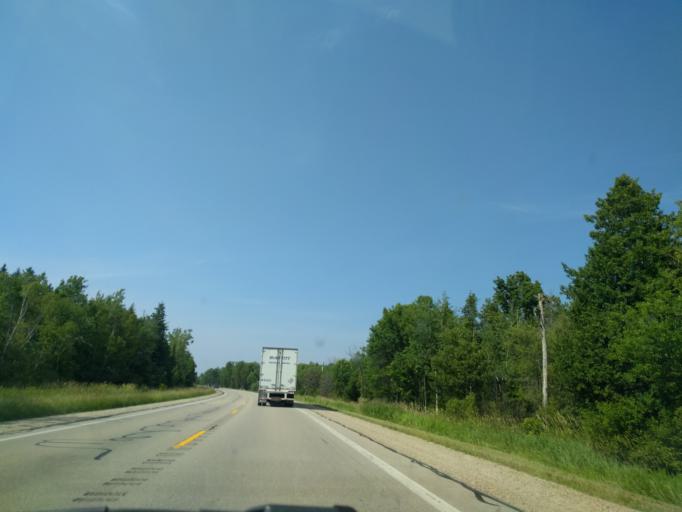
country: US
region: Michigan
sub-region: Delta County
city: Escanaba
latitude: 45.5074
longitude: -87.2878
